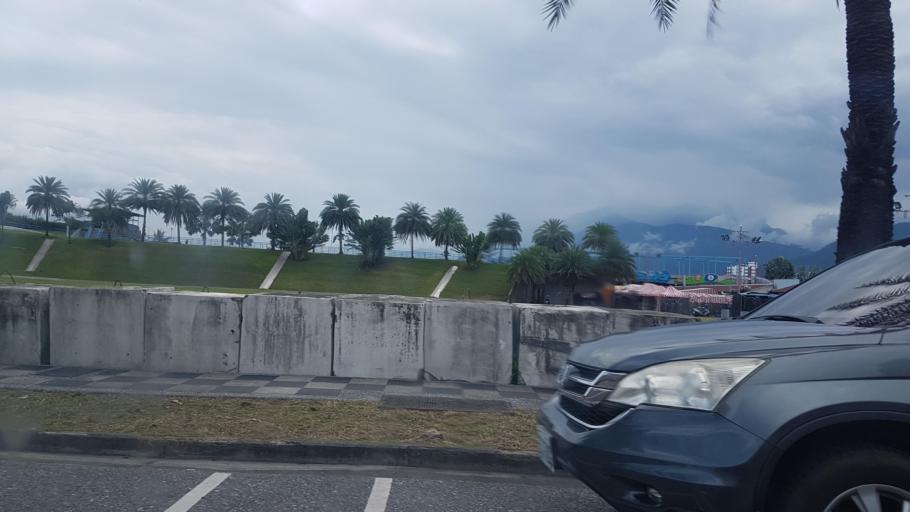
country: TW
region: Taiwan
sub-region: Hualien
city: Hualian
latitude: 23.9721
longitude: 121.6131
